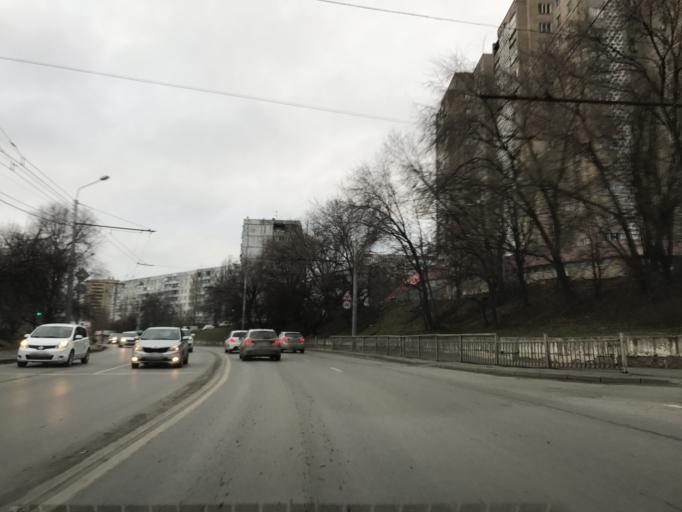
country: RU
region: Rostov
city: Severnyy
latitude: 47.2979
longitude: 39.7237
